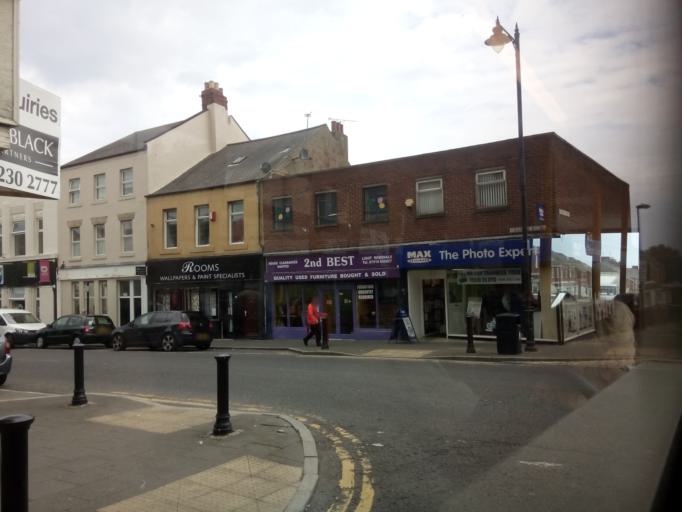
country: GB
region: England
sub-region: Borough of North Tyneside
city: North Shields
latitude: 55.0074
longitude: -1.4468
